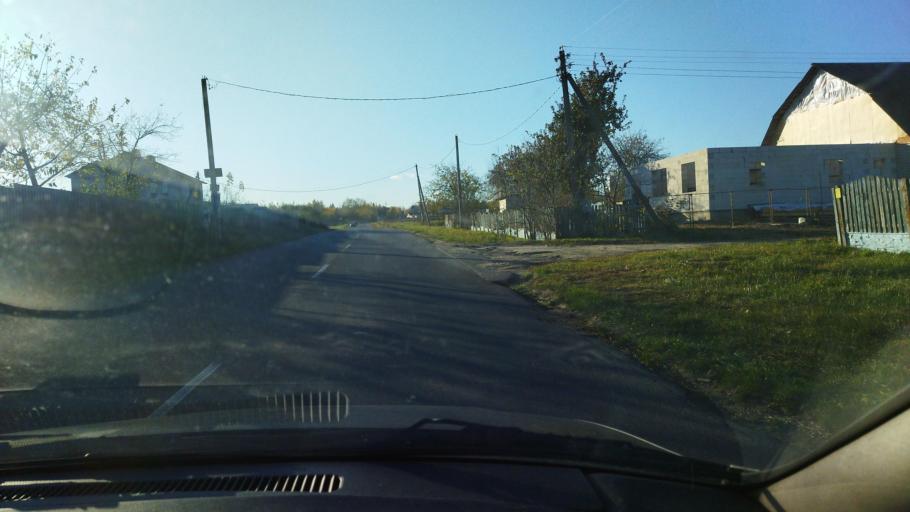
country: BY
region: Minsk
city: Kalodzishchy
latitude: 53.9463
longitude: 27.8356
